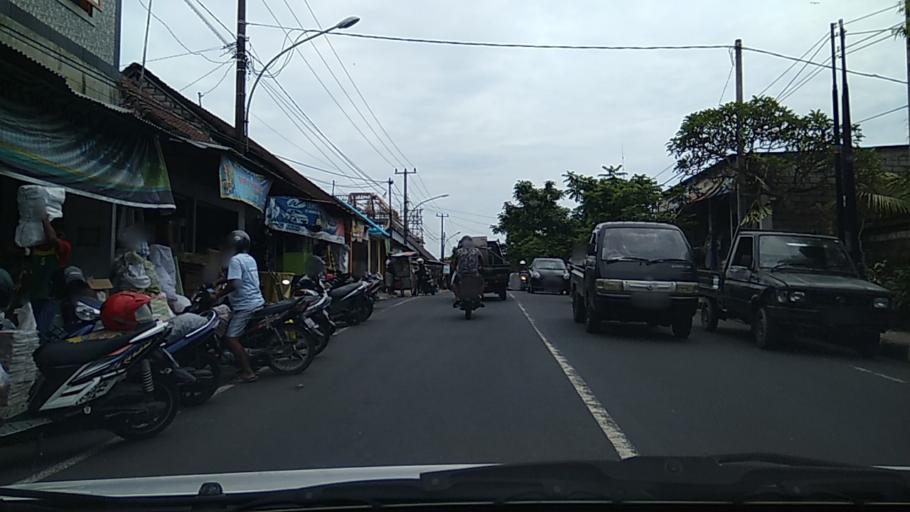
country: ID
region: Bali
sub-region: Kabupaten Gianyar
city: Ubud
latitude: -8.5349
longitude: 115.3130
